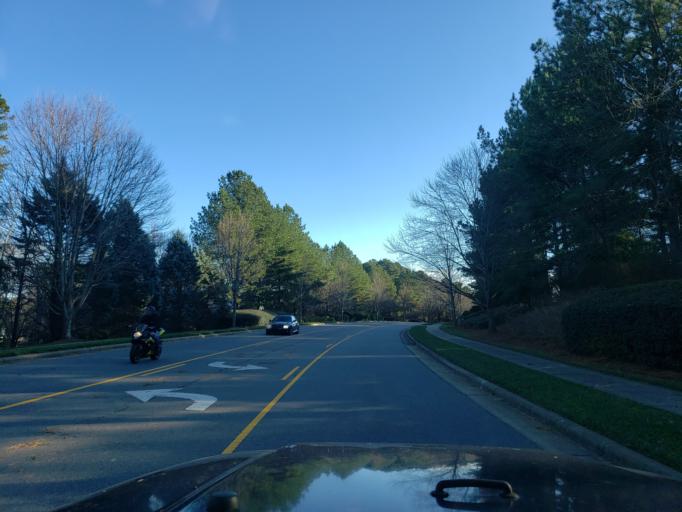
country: US
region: North Carolina
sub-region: Catawba County
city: Lake Norman of Catawba
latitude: 35.5434
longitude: -80.9176
